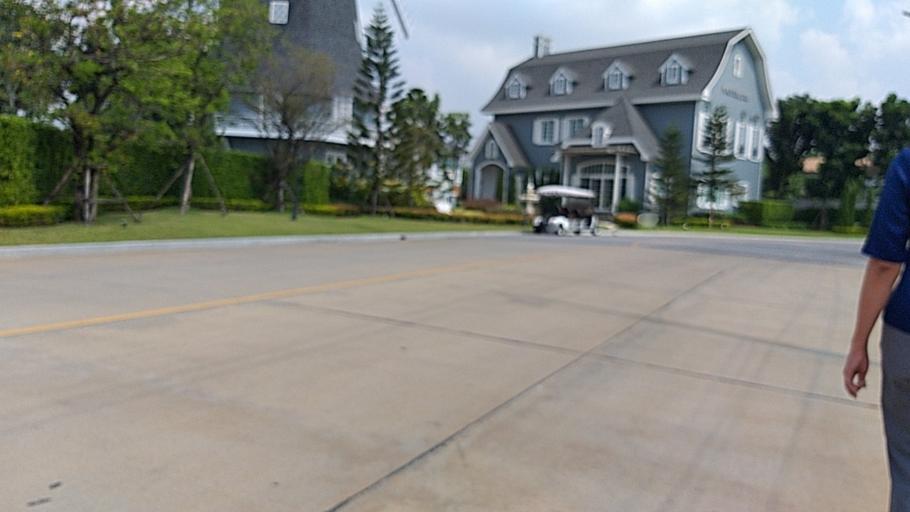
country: TH
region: Pathum Thani
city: Ban Rangsit
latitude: 14.0342
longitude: 100.7644
